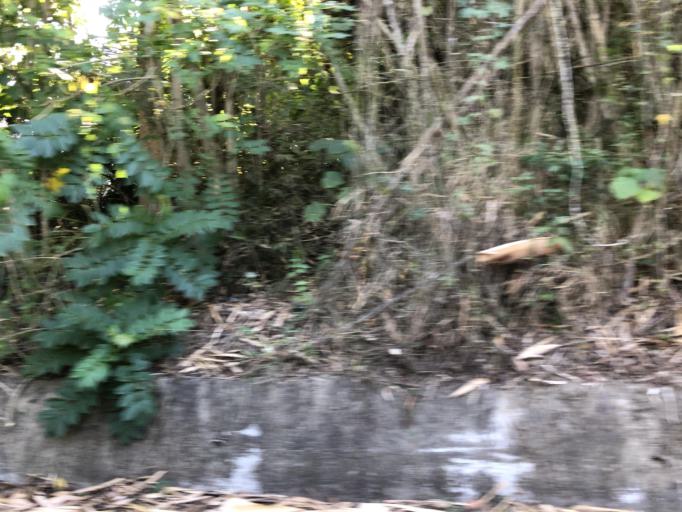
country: TW
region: Taiwan
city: Yujing
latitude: 23.0222
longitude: 120.3839
